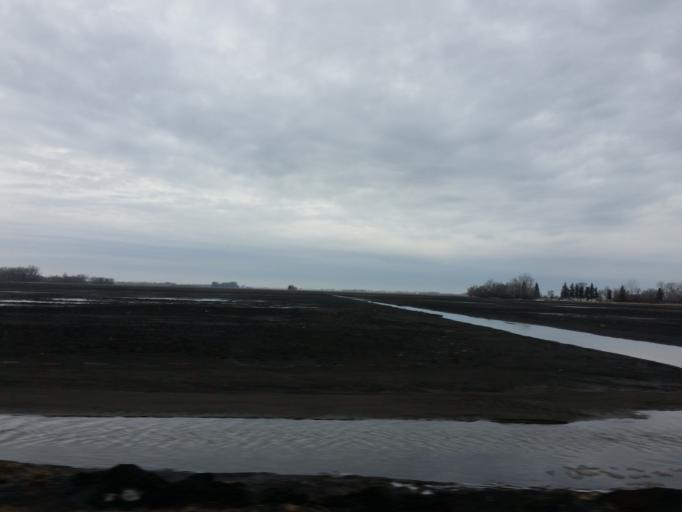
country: US
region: North Dakota
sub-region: Walsh County
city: Grafton
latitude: 48.3947
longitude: -97.4703
